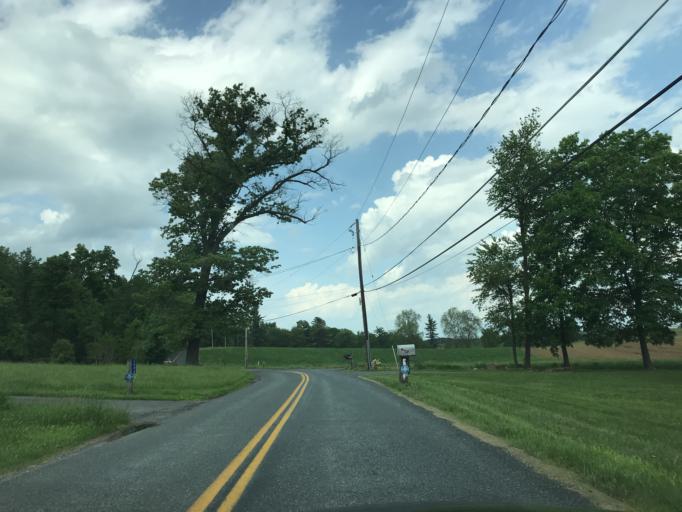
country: US
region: Pennsylvania
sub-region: York County
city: Susquehanna Trails
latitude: 39.7056
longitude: -76.3288
